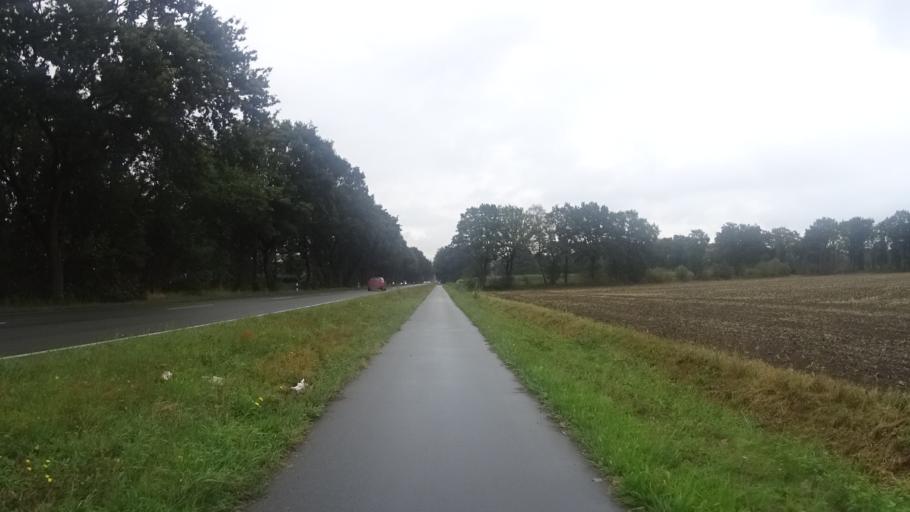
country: DE
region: Lower Saxony
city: Holtland
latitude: 53.2842
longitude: 7.5793
